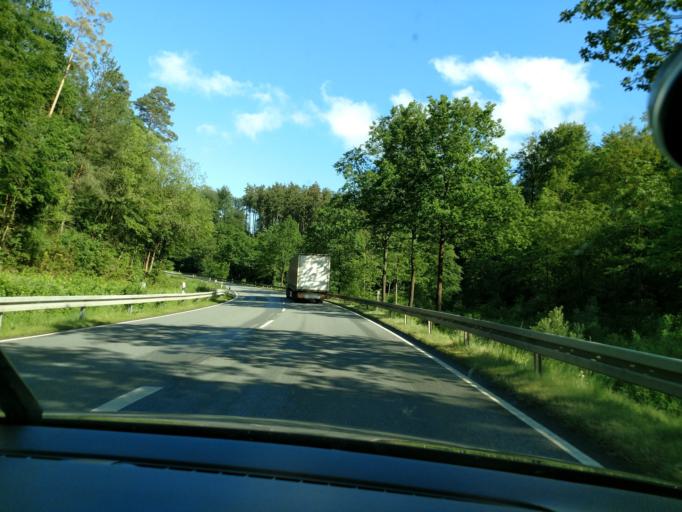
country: DE
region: Hesse
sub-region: Regierungsbezirk Kassel
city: Bad Arolsen
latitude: 51.3552
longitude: 9.0056
